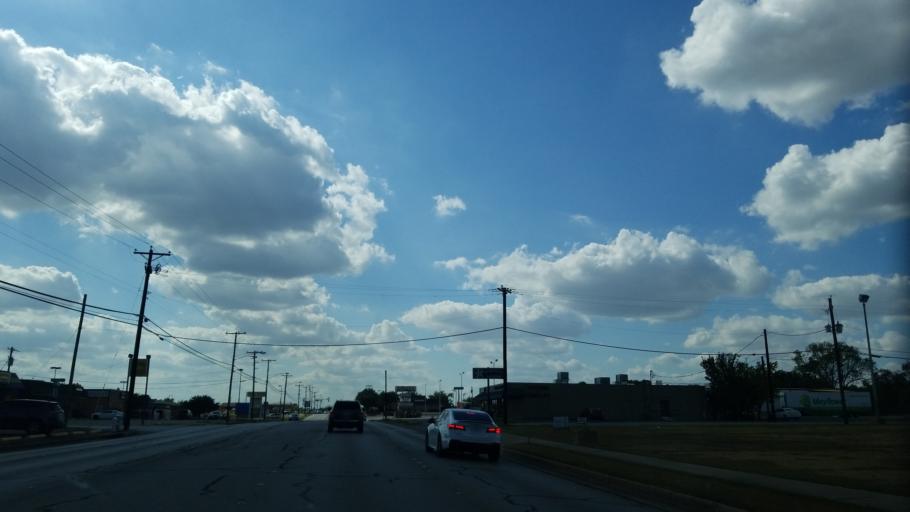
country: US
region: Texas
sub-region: Tarrant County
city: Hurst
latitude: 32.8340
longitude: -97.1733
